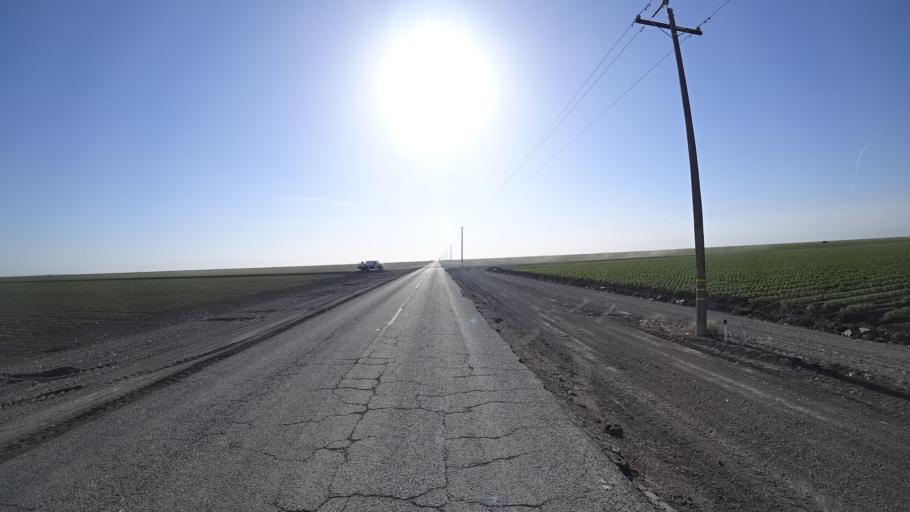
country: US
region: California
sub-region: Kings County
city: Stratford
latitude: 36.0797
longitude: -119.7722
